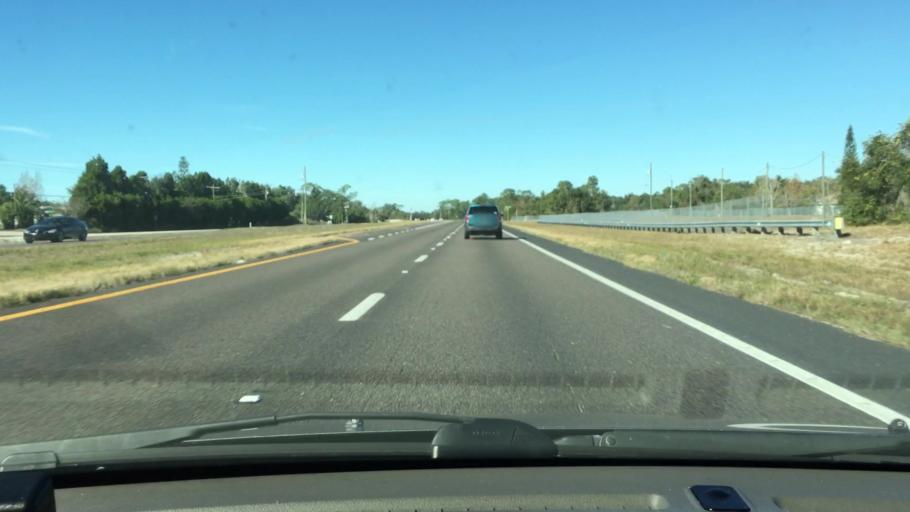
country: US
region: Florida
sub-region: Osceola County
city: Saint Cloud
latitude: 28.2373
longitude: -81.1936
